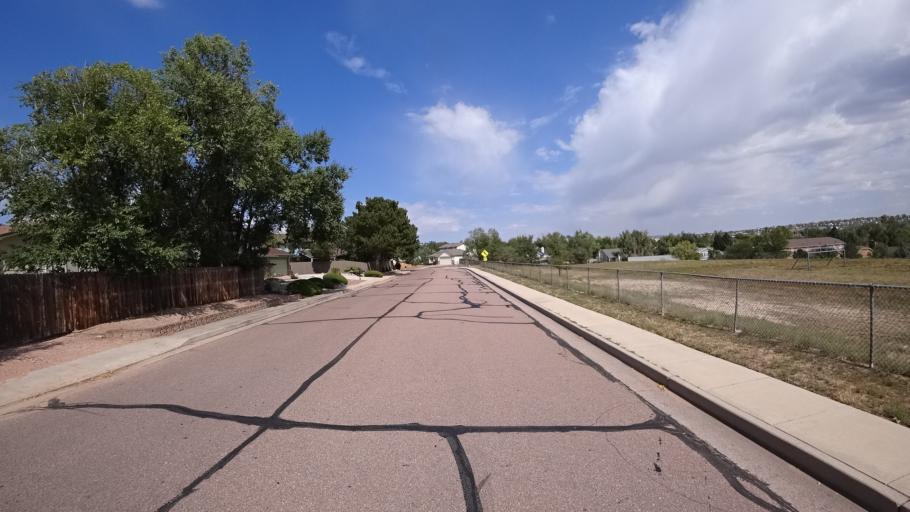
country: US
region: Colorado
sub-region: El Paso County
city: Cimarron Hills
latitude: 38.8572
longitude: -104.7278
